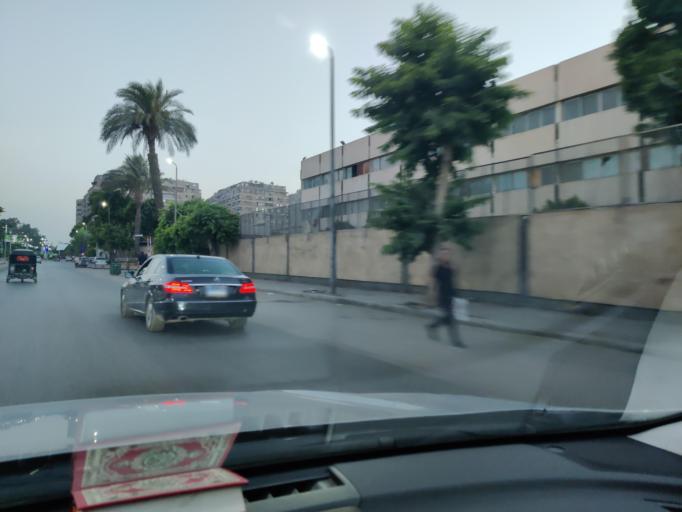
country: EG
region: Muhafazat al Qahirah
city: Cairo
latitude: 30.1048
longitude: 31.3021
